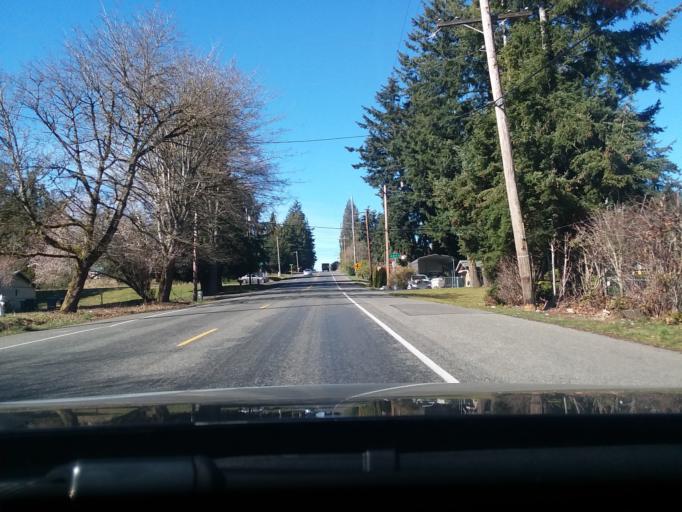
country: US
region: Washington
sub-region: Pierce County
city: Summit
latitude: 47.1620
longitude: -122.3430
